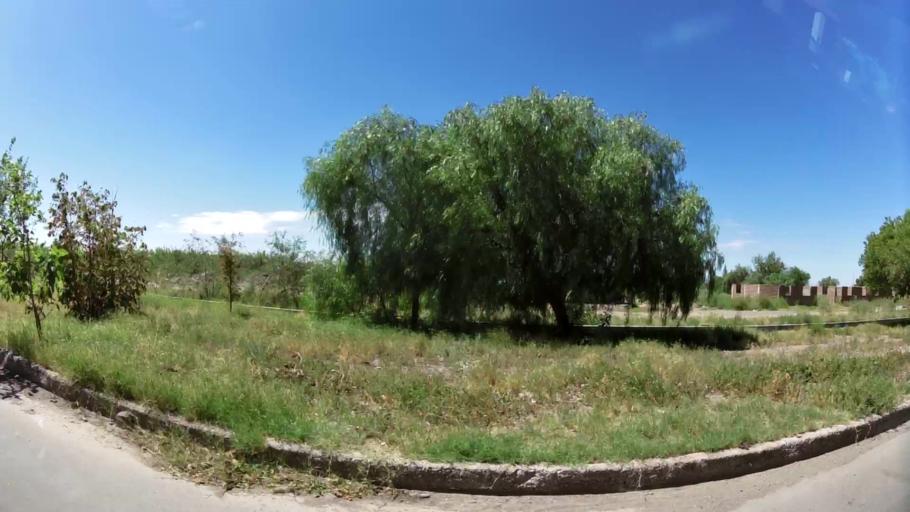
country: AR
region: Mendoza
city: Las Heras
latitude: -32.8383
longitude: -68.8629
